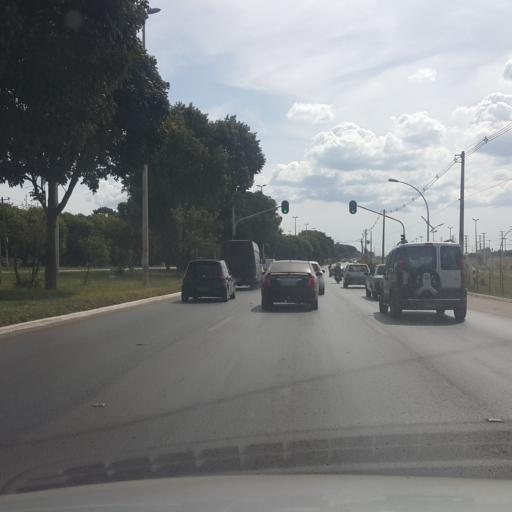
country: BR
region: Federal District
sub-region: Brasilia
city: Brasilia
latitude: -15.8056
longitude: -48.0579
